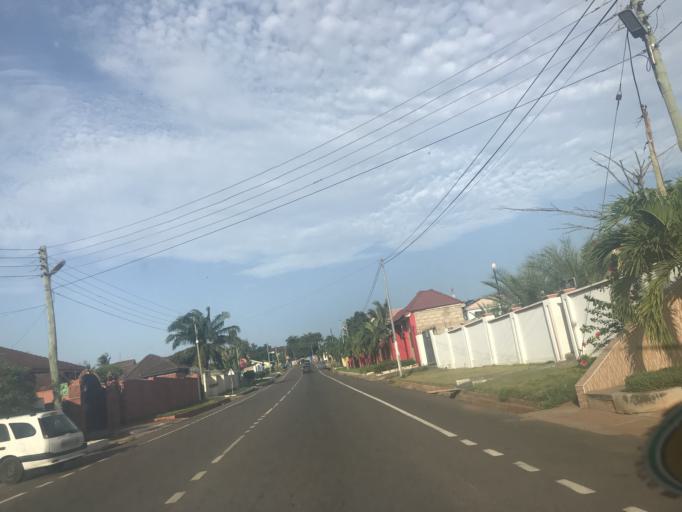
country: GH
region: Greater Accra
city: Medina Estates
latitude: 5.6688
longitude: -0.1803
